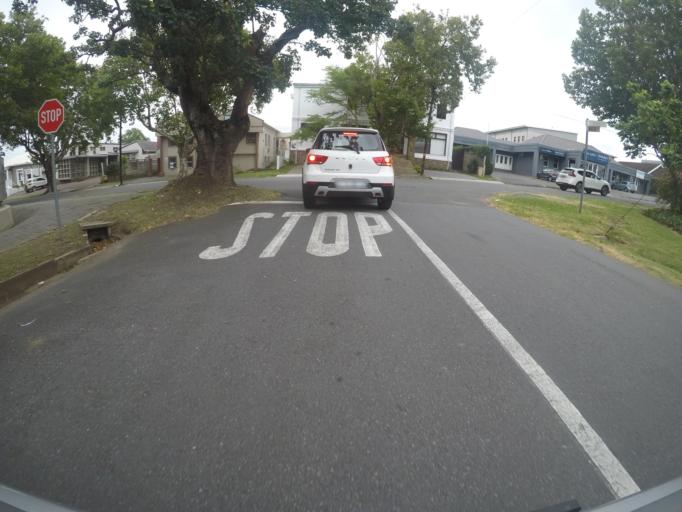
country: ZA
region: Eastern Cape
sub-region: Buffalo City Metropolitan Municipality
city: East London
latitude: -32.9802
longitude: 27.9025
